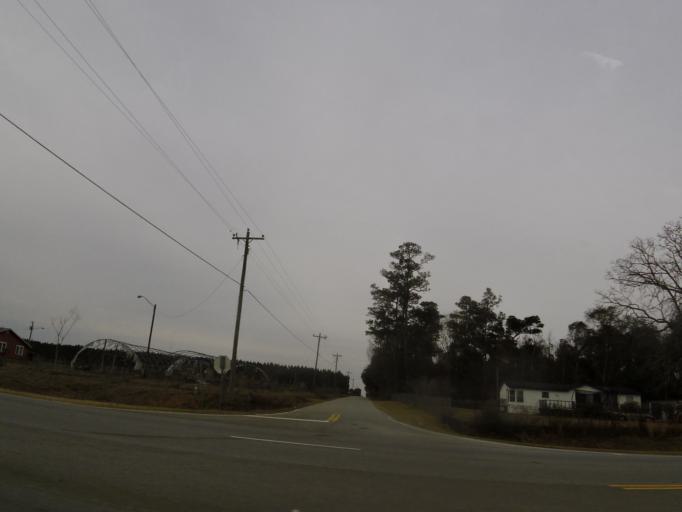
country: US
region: Georgia
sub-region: Grady County
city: Cairo
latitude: 30.8688
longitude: -84.1335
